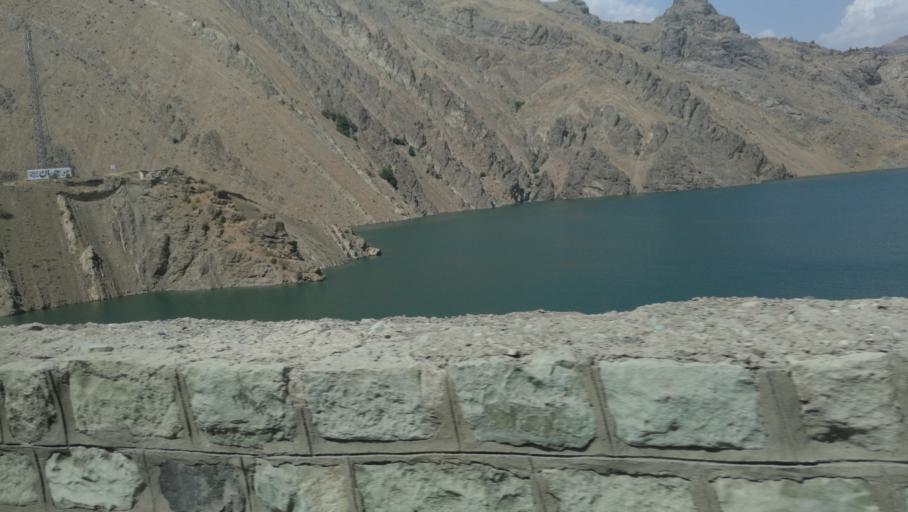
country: IR
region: Alborz
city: Karaj
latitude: 35.9769
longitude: 51.0956
